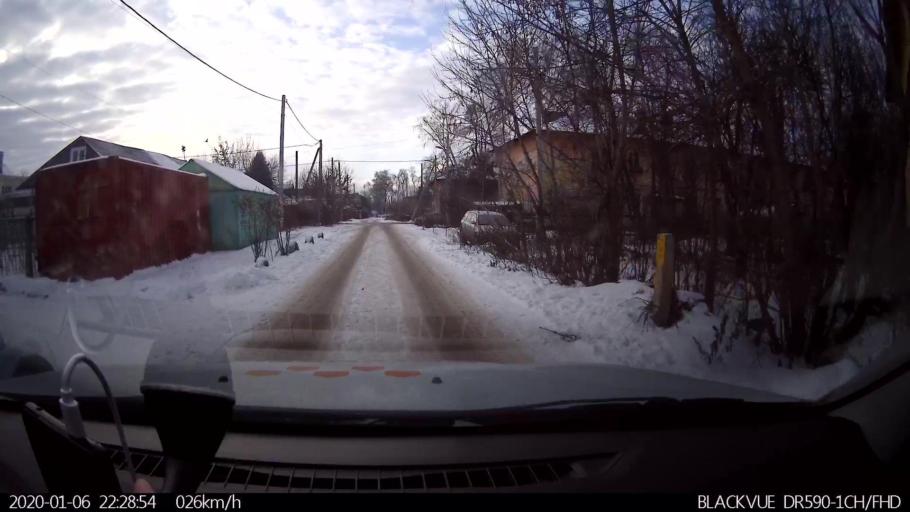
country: RU
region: Nizjnij Novgorod
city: Burevestnik
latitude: 56.2257
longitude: 43.8416
